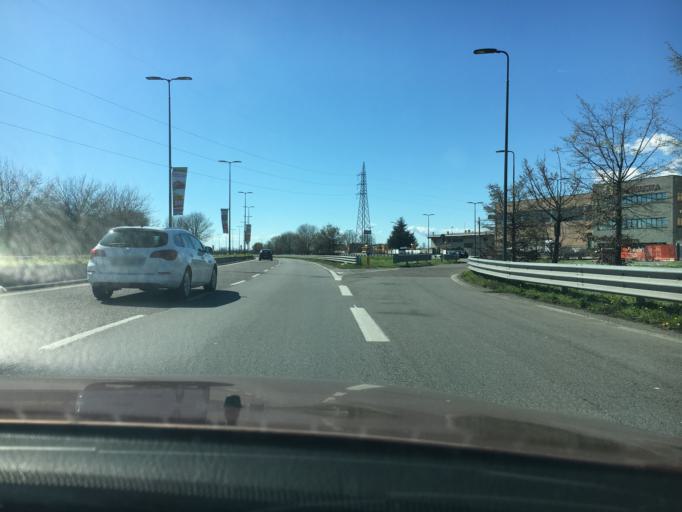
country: IT
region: Lombardy
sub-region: Citta metropolitana di Milano
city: Settimo Milanese
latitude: 45.4572
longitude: 9.0689
